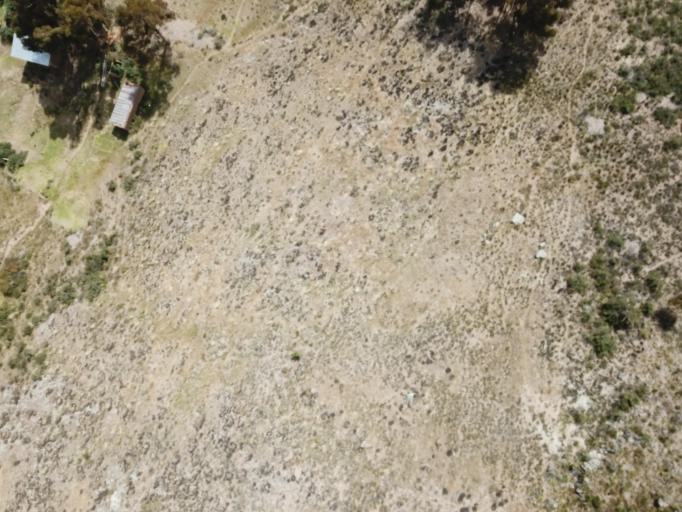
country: BO
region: La Paz
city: Achacachi
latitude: -16.0557
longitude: -68.8097
